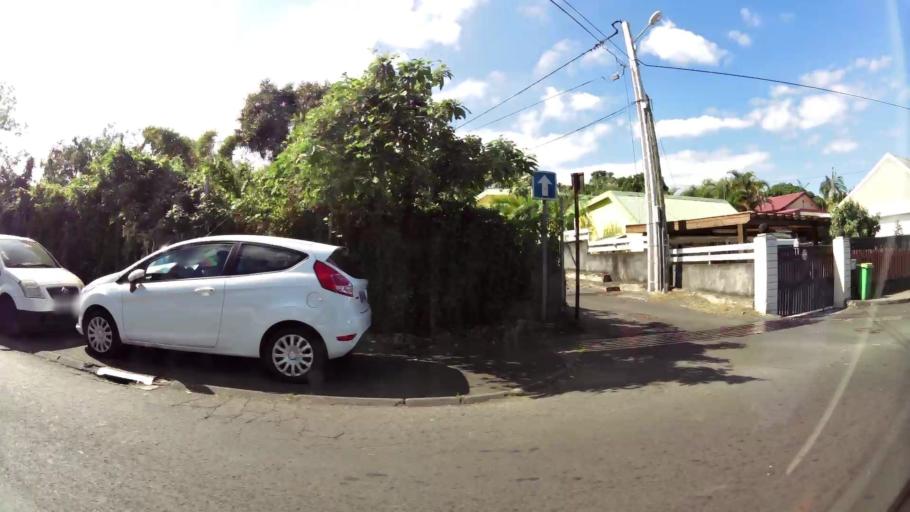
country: RE
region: Reunion
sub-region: Reunion
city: Le Tampon
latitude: -21.2904
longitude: 55.5100
